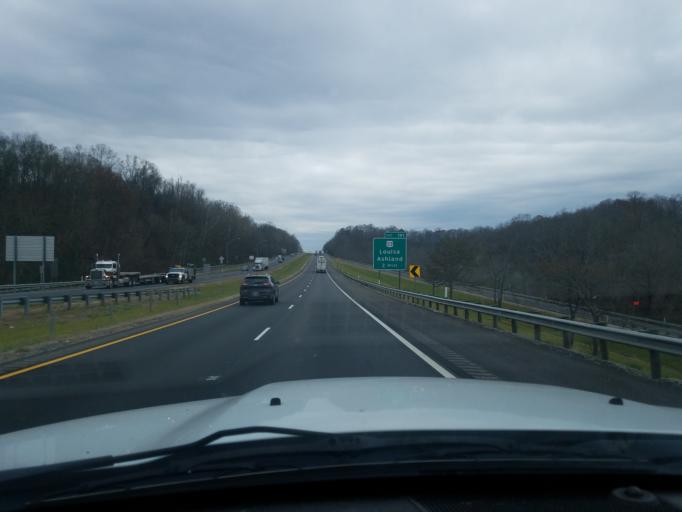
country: US
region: West Virginia
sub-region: Wayne County
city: Kenova
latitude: 38.3908
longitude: -82.5745
